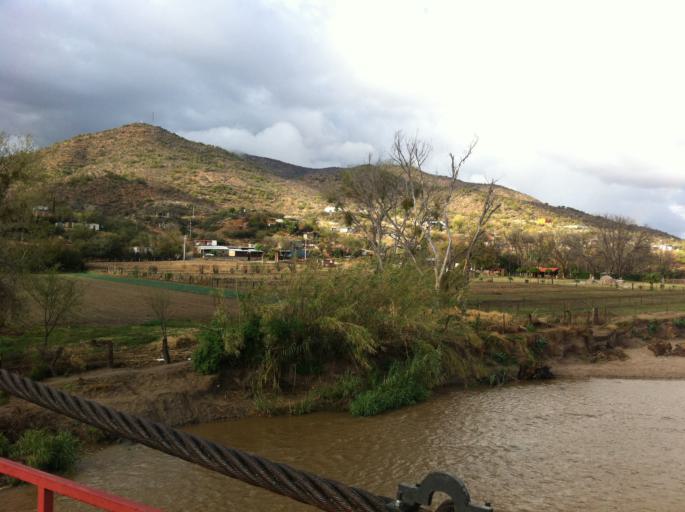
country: MX
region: Sonora
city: Magdalena de Kino
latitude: 30.6313
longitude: -110.9748
